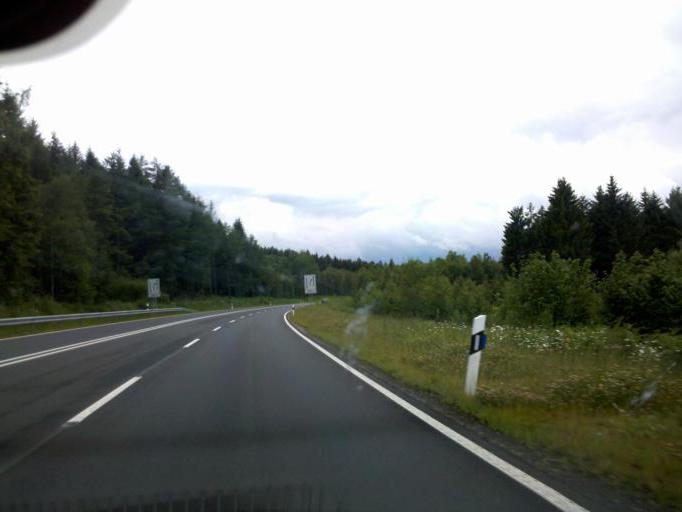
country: DE
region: North Rhine-Westphalia
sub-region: Regierungsbezirk Arnsberg
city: Olpe
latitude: 51.0561
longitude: 7.9093
